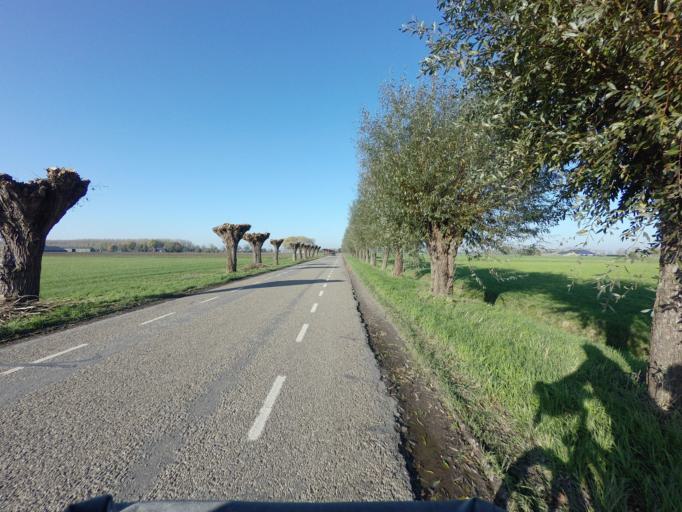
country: NL
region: North Brabant
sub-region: Gemeente Waalwijk
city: Waalwijk
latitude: 51.7547
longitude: 5.0549
